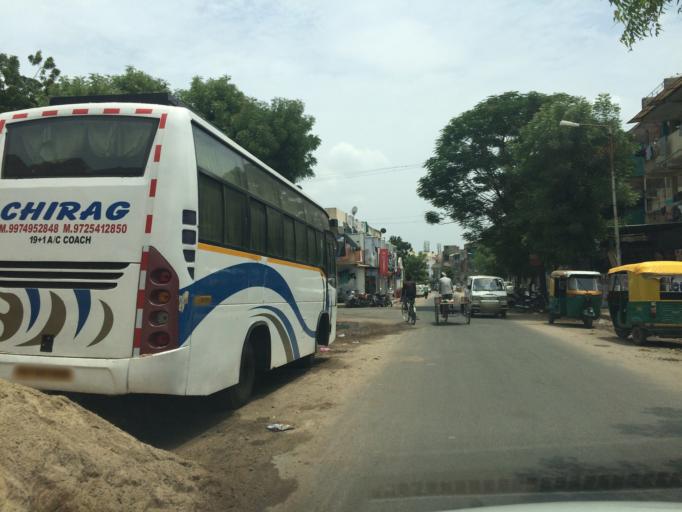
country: IN
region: Gujarat
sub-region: Ahmadabad
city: Ahmedabad
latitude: 23.0789
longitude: 72.5641
